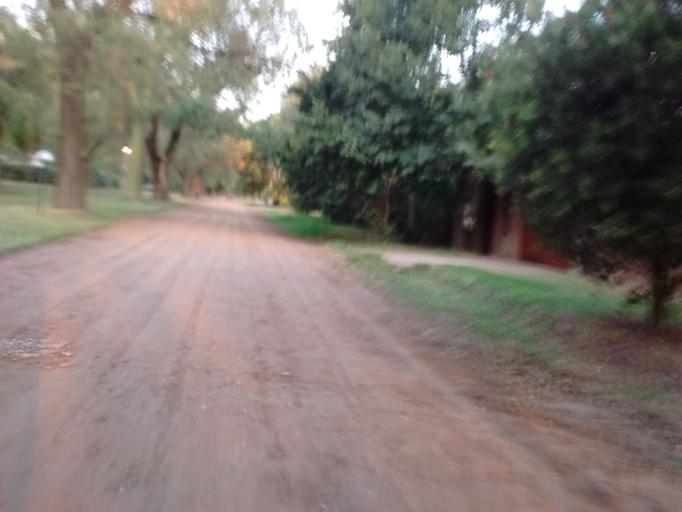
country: AR
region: Santa Fe
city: Funes
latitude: -32.9232
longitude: -60.8403
